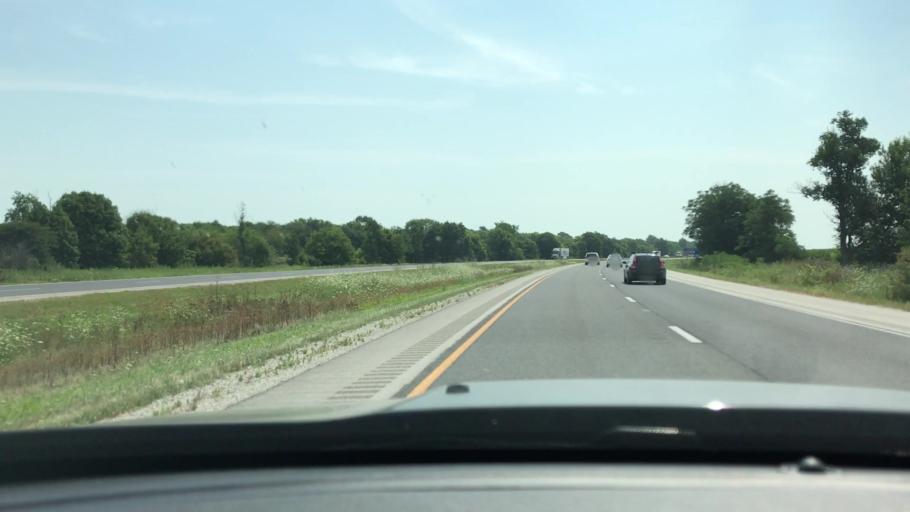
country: US
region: Illinois
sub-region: Henry County
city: Kewanee
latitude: 41.4161
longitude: -89.9350
